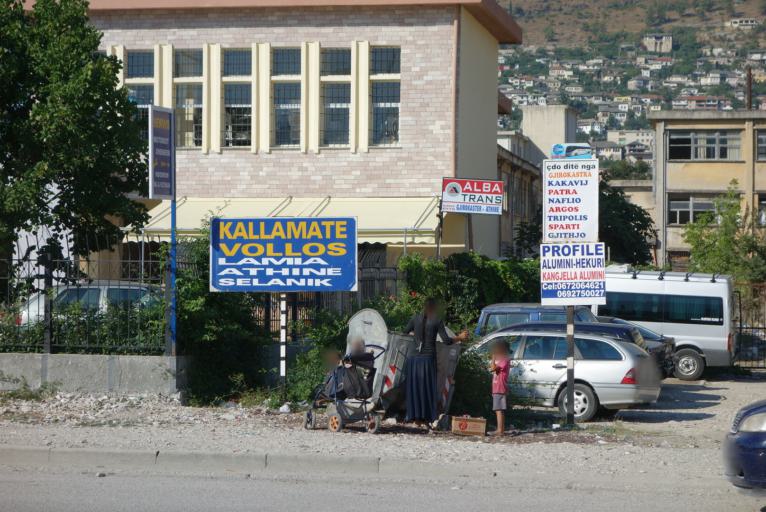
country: AL
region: Gjirokaster
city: Gjirokaster
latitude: 40.0836
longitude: 20.1452
